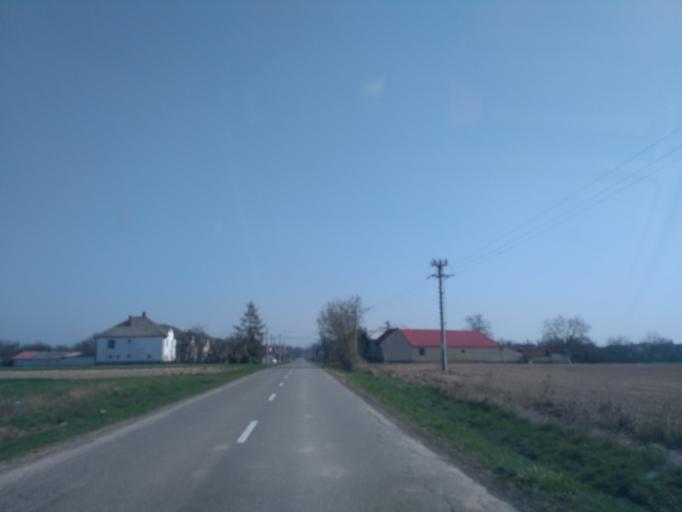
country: SK
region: Kosicky
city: Secovce
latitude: 48.7764
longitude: 21.6787
